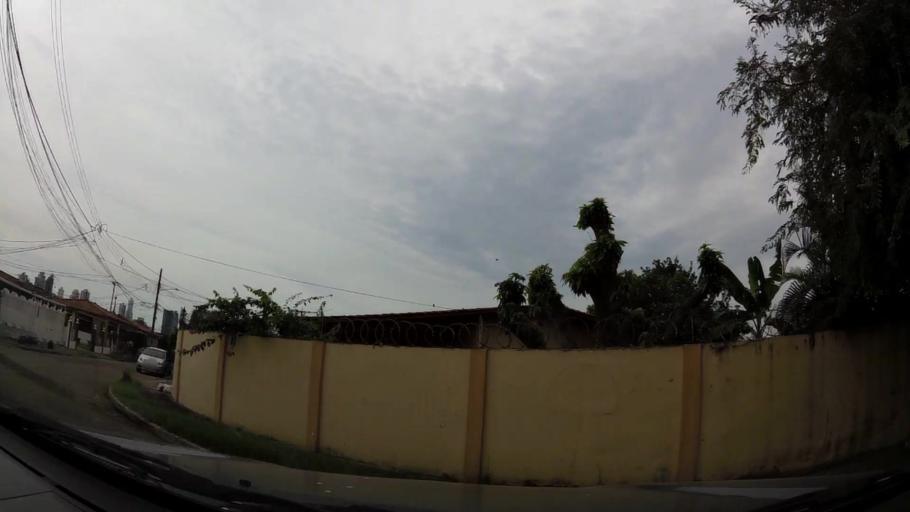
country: PA
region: Panama
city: San Miguelito
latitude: 9.0283
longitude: -79.4695
